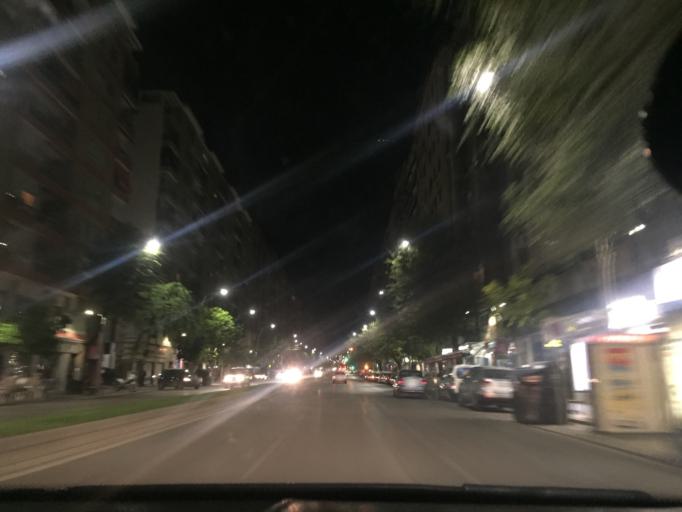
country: ES
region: Andalusia
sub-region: Provincia de Jaen
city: Jaen
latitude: 37.7774
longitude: -3.7936
